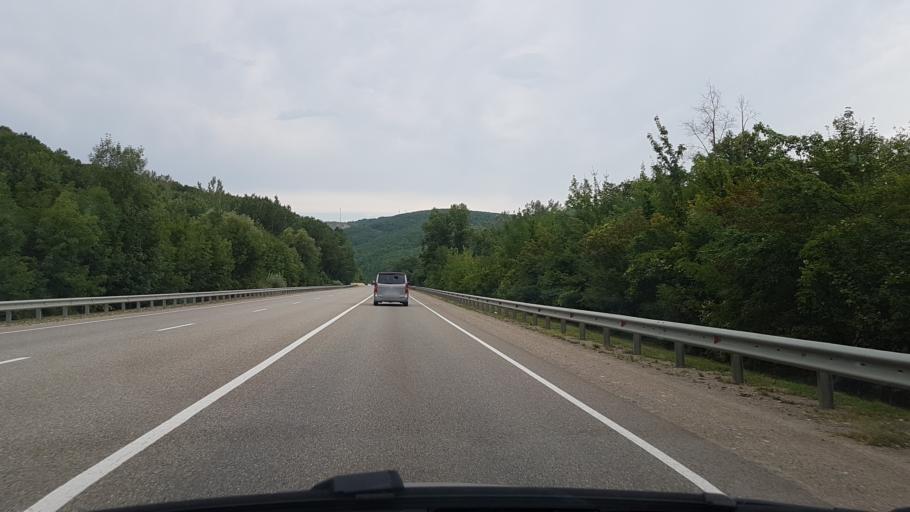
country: RU
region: Krasnodarskiy
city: Goryachiy Klyuch
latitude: 44.5878
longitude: 39.0096
